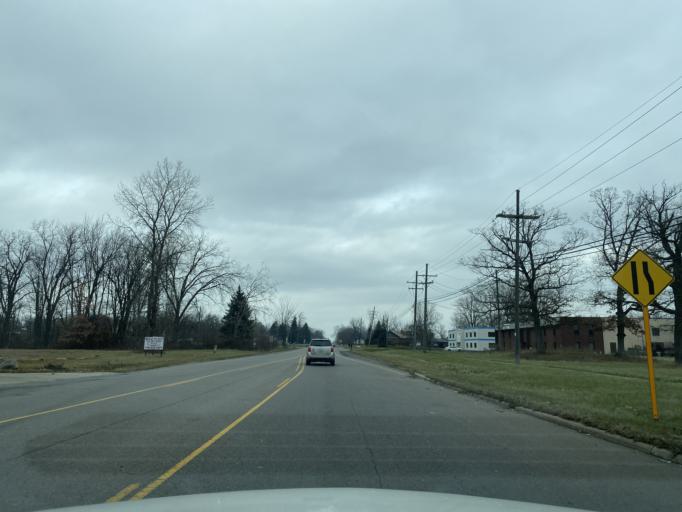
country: US
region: Michigan
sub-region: Wayne County
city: Taylor
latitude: 42.2123
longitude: -83.2878
